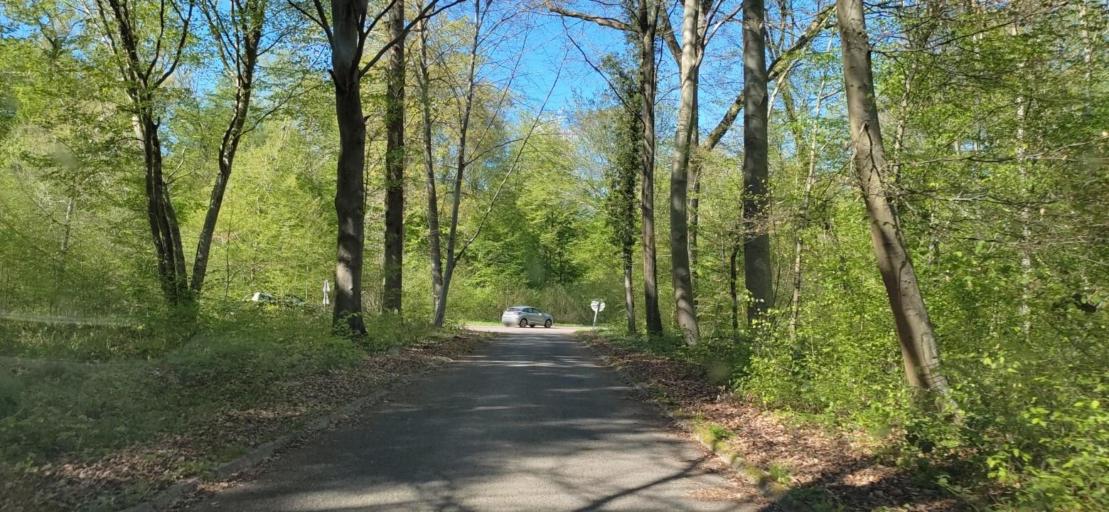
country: FR
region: Picardie
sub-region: Departement de l'Oise
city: Choisy-au-Bac
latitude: 49.4299
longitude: 2.9075
